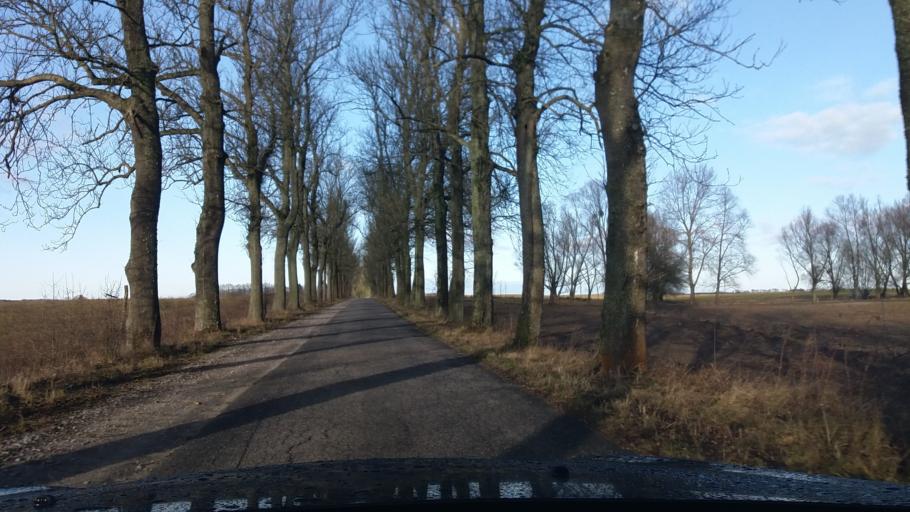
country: PL
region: West Pomeranian Voivodeship
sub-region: Powiat choszczenski
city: Drawno
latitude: 53.1849
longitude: 15.7981
